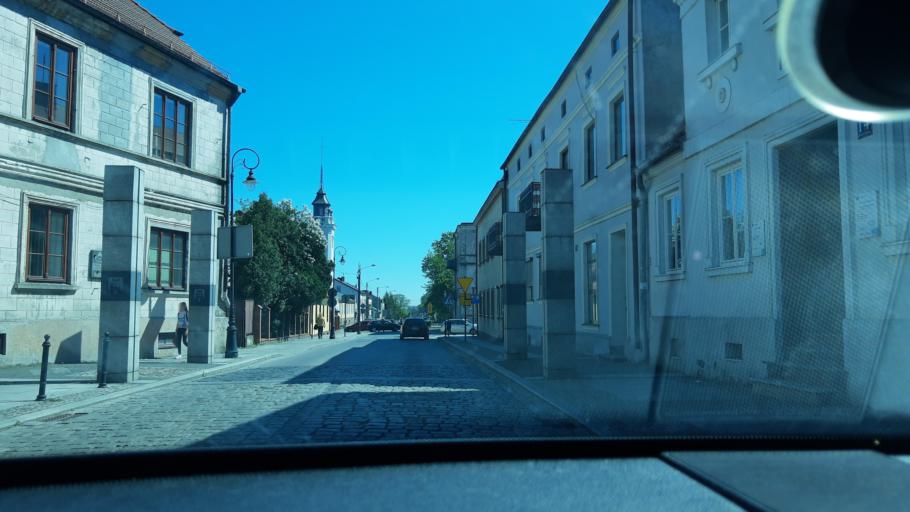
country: PL
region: Lodz Voivodeship
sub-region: Powiat sieradzki
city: Sieradz
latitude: 51.5925
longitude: 18.7382
